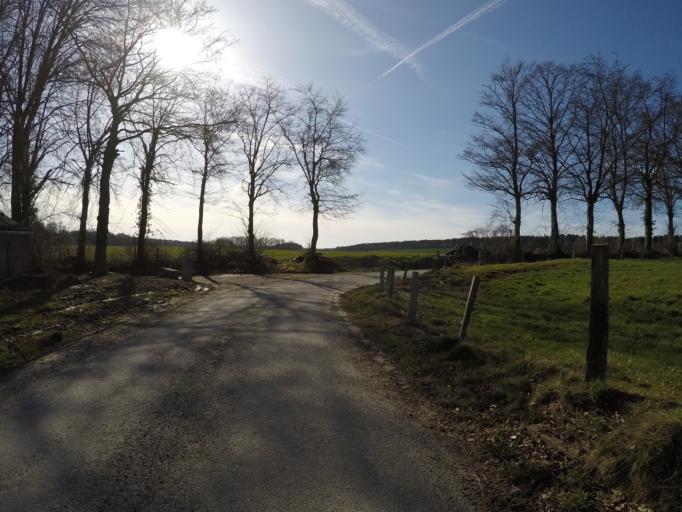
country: BE
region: Wallonia
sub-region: Province de Namur
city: Hamois
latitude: 50.3503
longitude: 5.1120
